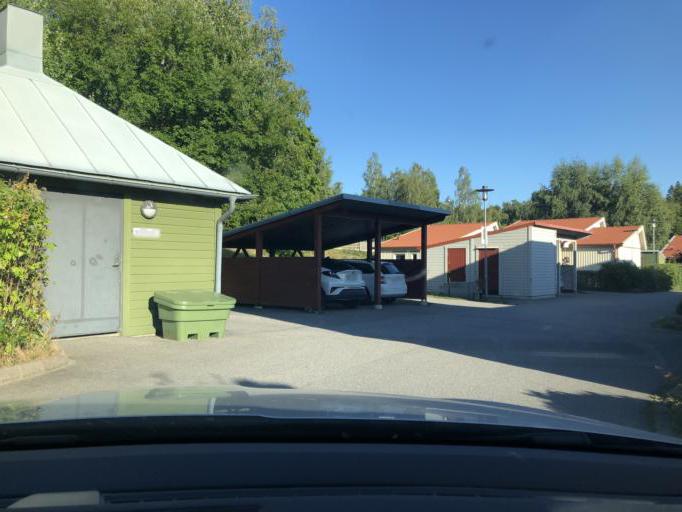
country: SE
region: Stockholm
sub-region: Sodertalje Kommun
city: Soedertaelje
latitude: 59.1834
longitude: 17.6159
